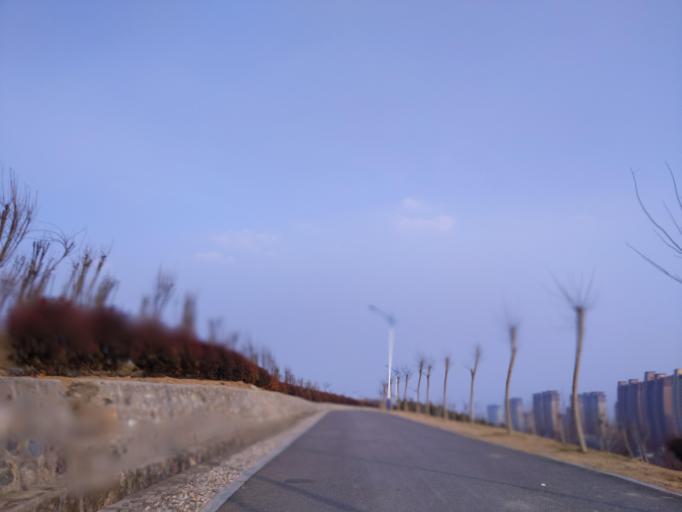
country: CN
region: Henan Sheng
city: Puyang
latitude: 35.8194
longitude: 115.0133
